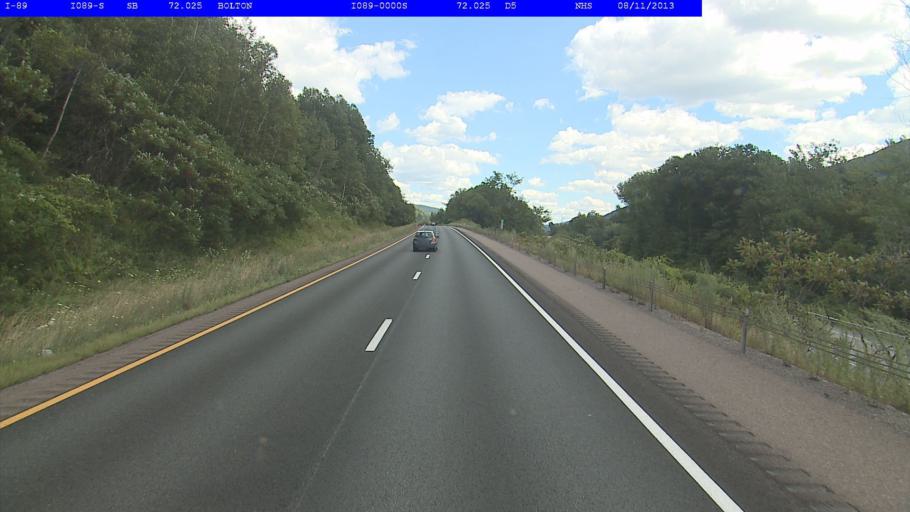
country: US
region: Vermont
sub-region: Chittenden County
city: Jericho
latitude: 44.3787
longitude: -72.9070
